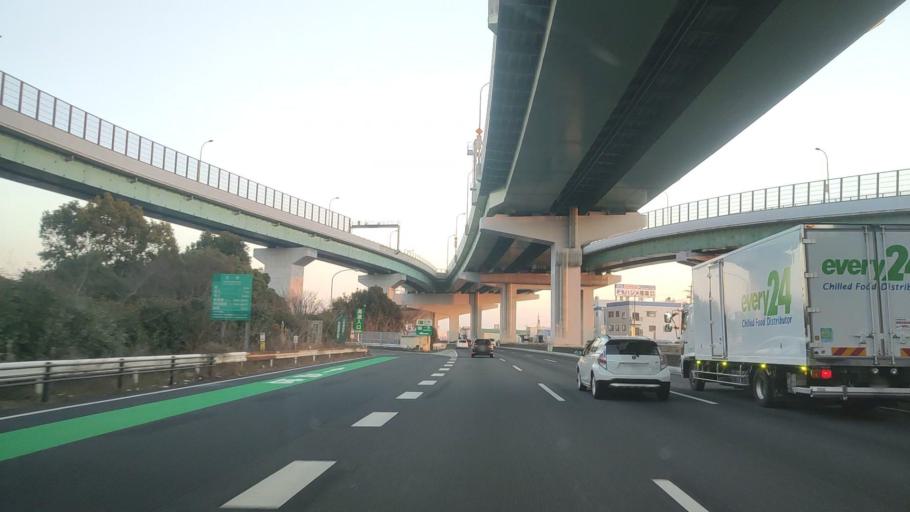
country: JP
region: Aichi
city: Iwakura
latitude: 35.2710
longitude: 136.8319
